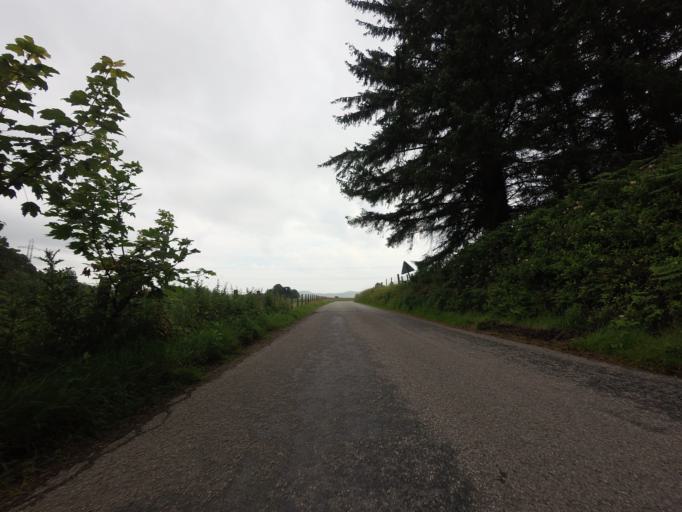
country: GB
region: Scotland
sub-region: Highland
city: Evanton
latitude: 57.8859
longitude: -4.3866
